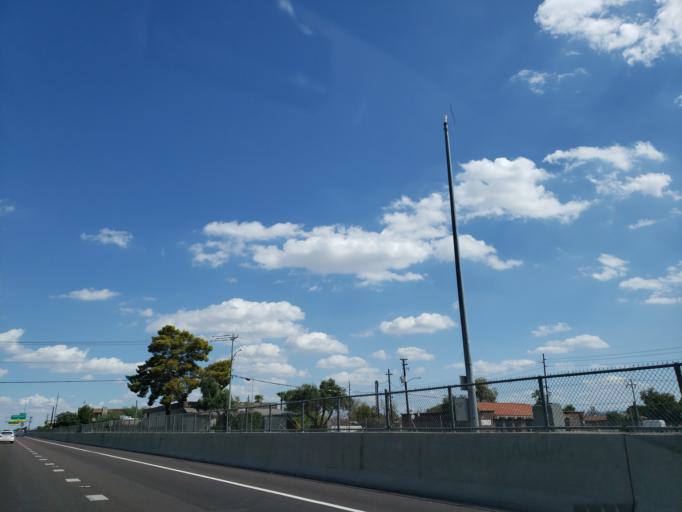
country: US
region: Arizona
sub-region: Maricopa County
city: Phoenix
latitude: 33.4863
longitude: -112.1129
